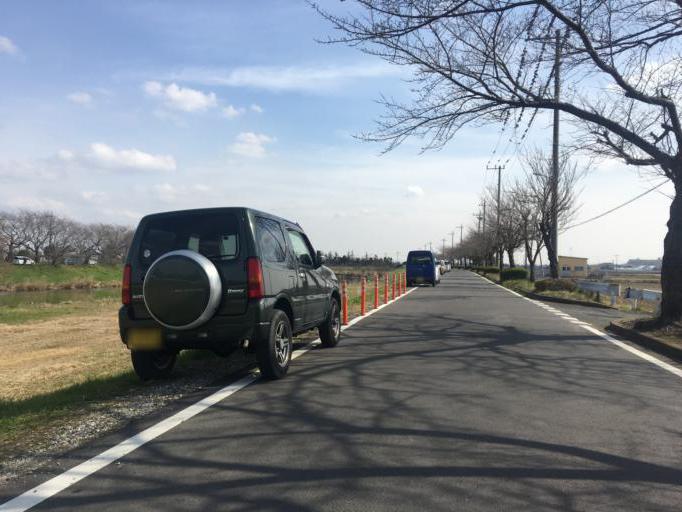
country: JP
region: Saitama
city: Kamifukuoka
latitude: 35.8749
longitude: 139.5571
